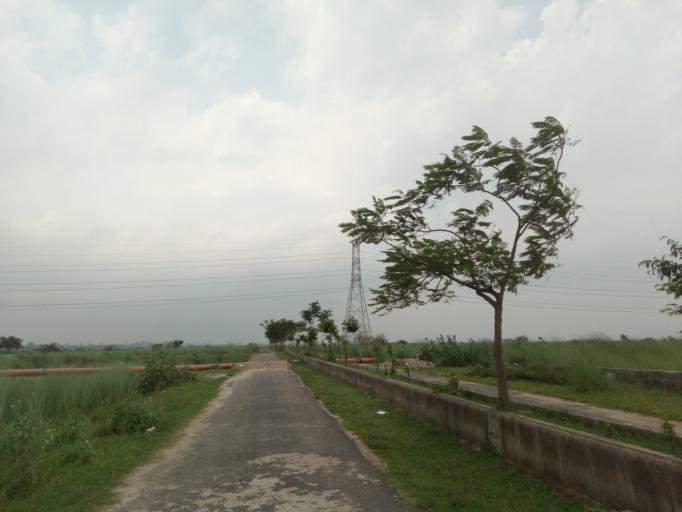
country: BD
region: Dhaka
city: Paltan
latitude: 23.7691
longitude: 90.4492
